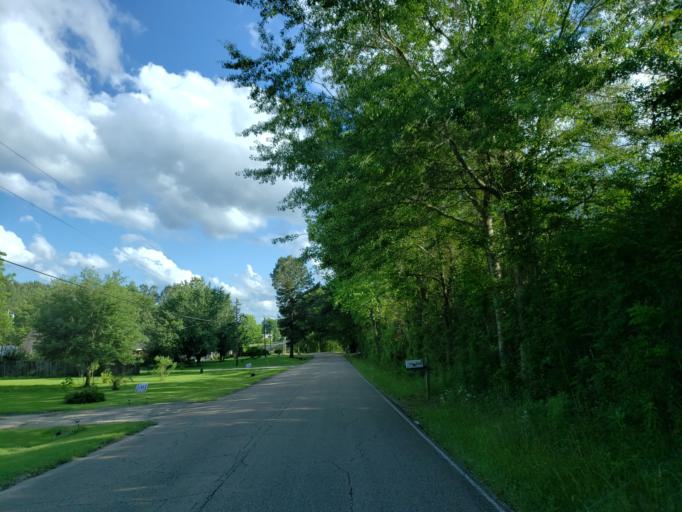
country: US
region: Mississippi
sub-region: Forrest County
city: Petal
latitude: 31.3197
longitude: -89.1971
